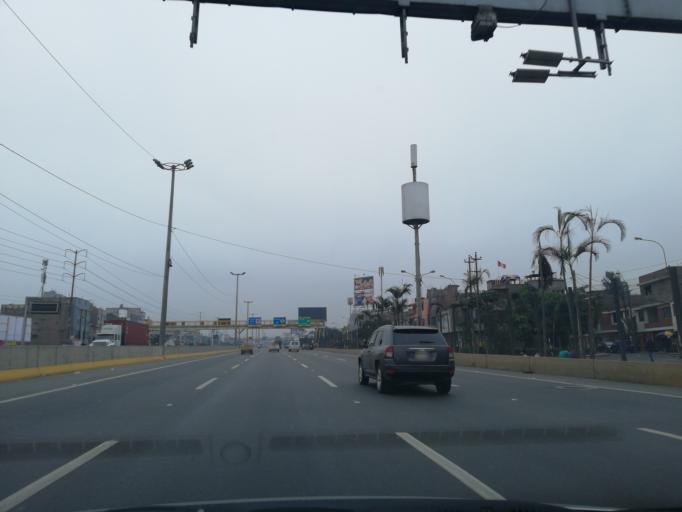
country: PE
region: Lima
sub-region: Lima
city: San Luis
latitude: -12.0772
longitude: -76.9755
